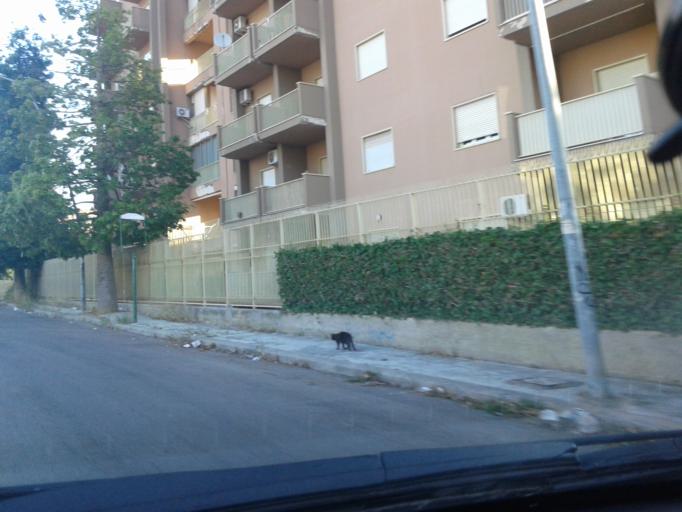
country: IT
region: Sicily
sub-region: Palermo
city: Ciaculli
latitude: 38.0831
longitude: 13.3621
